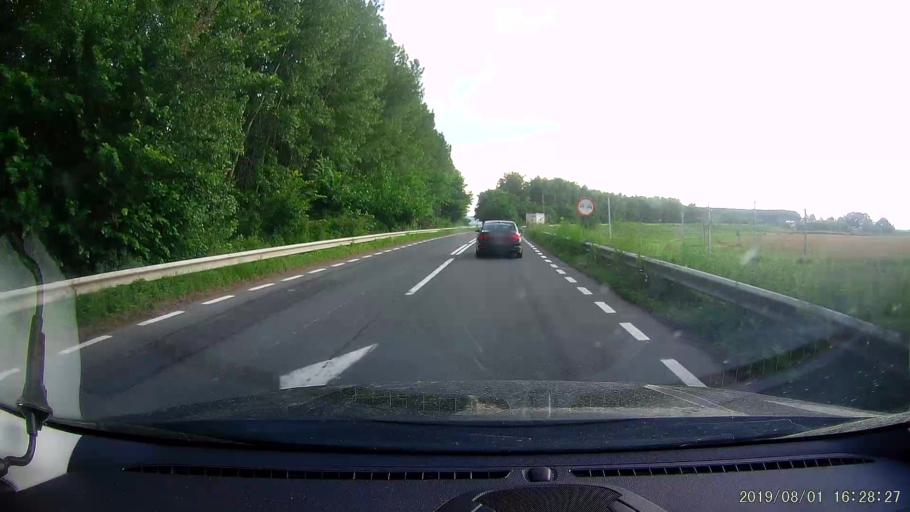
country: BG
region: Silistra
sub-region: Obshtina Silistra
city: Silistra
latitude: 44.1472
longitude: 27.3078
